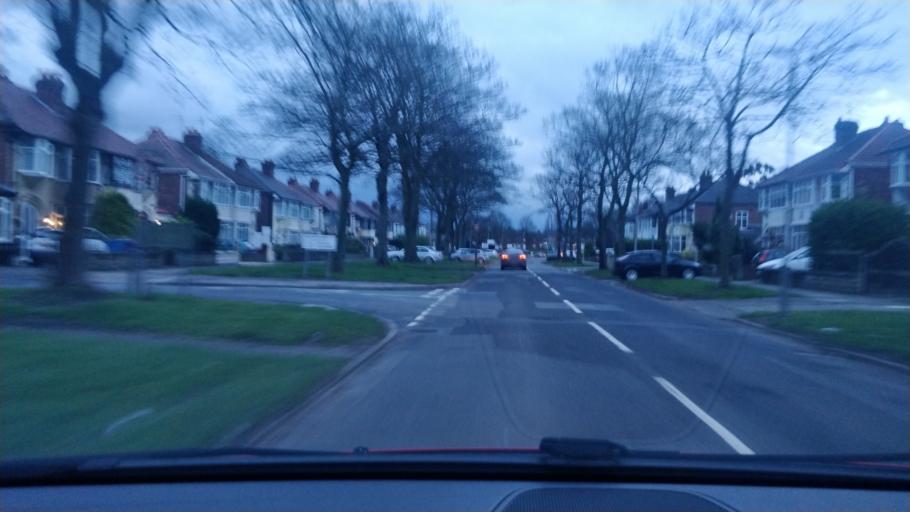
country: GB
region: England
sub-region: Knowsley
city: Knowsley
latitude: 53.4204
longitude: -2.8903
